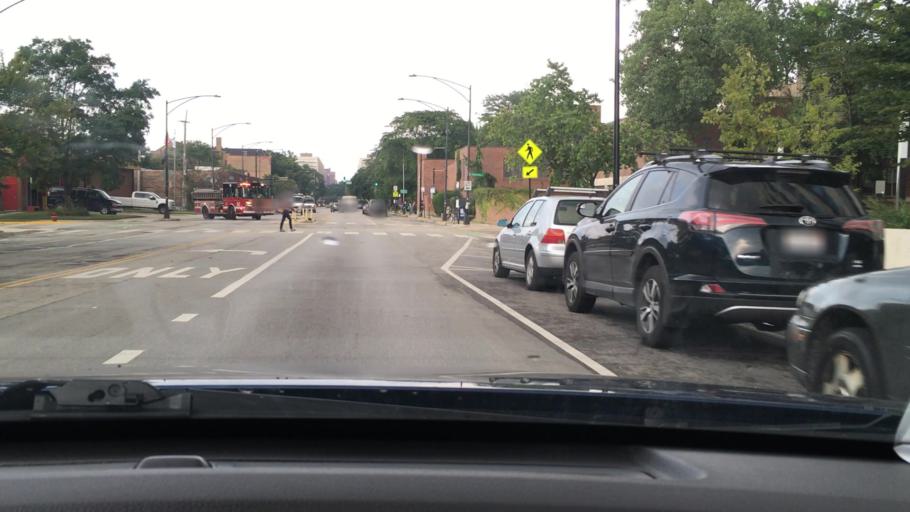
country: US
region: Illinois
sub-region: Cook County
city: Chicago
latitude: 41.7950
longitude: -87.5987
